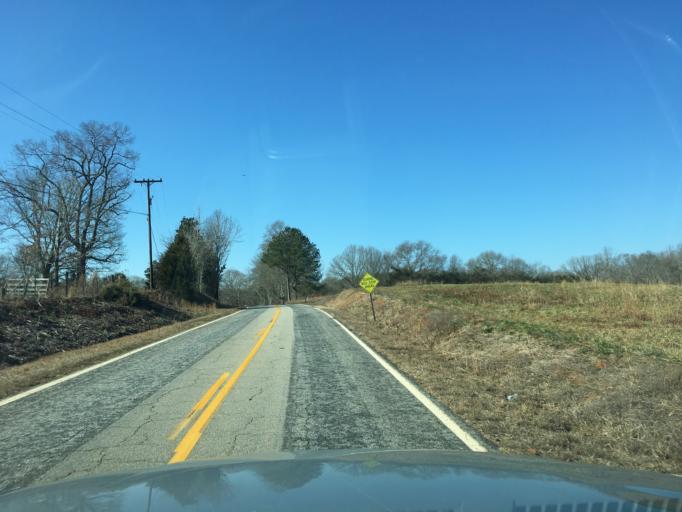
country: US
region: South Carolina
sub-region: Pickens County
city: Pickens
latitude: 34.8572
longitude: -82.7585
